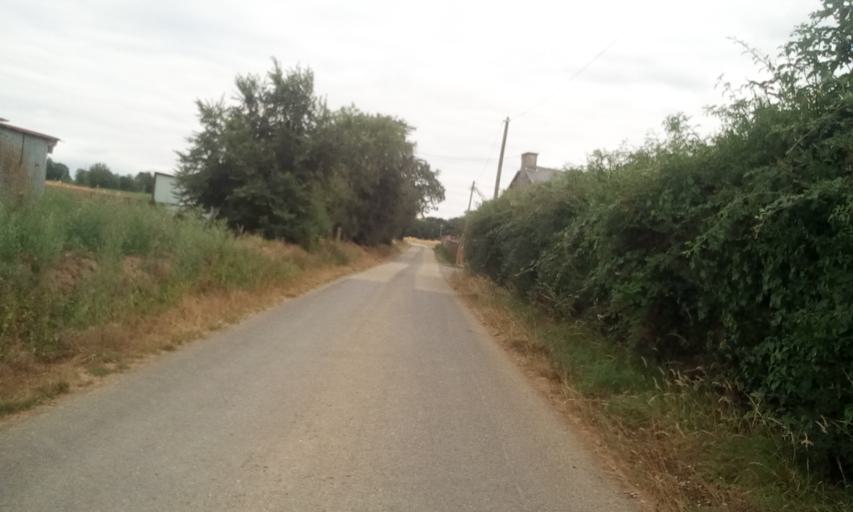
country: FR
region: Lower Normandy
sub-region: Departement du Calvados
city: Thury-Harcourt
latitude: 48.9884
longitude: -0.4276
